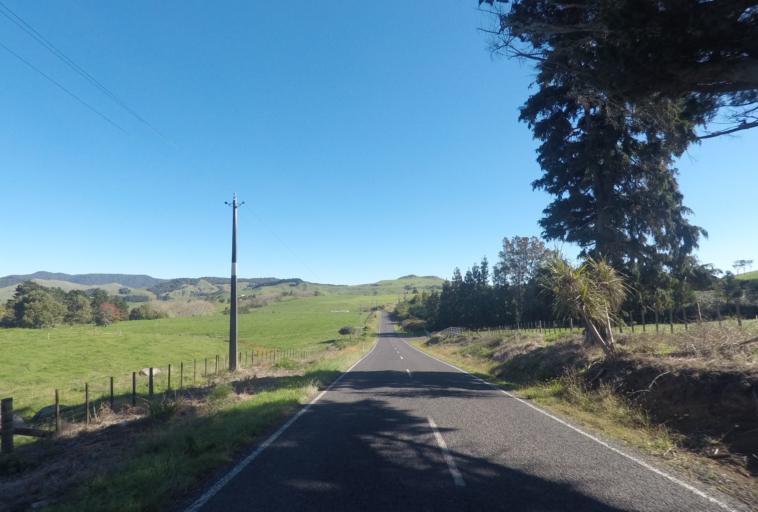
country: NZ
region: Bay of Plenty
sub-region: Western Bay of Plenty District
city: Waihi Beach
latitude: -37.3452
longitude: 175.8983
